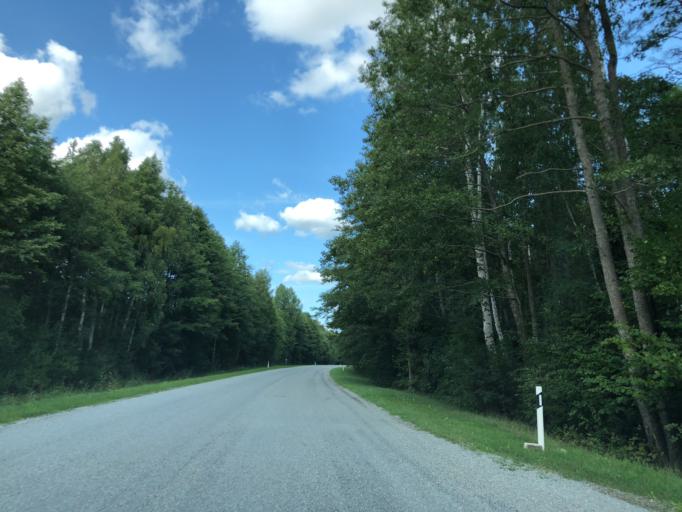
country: EE
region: Hiiumaa
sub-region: Kaerdla linn
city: Kardla
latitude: 58.8194
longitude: 22.7403
